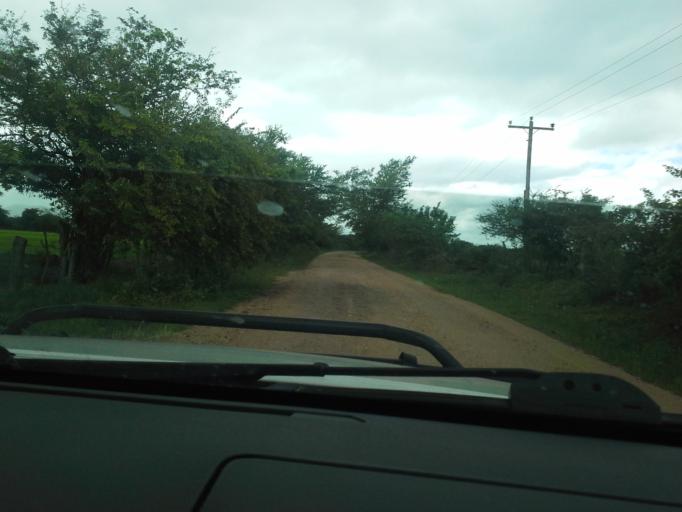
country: NI
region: Matagalpa
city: Ciudad Dario
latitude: 12.8226
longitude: -86.1958
